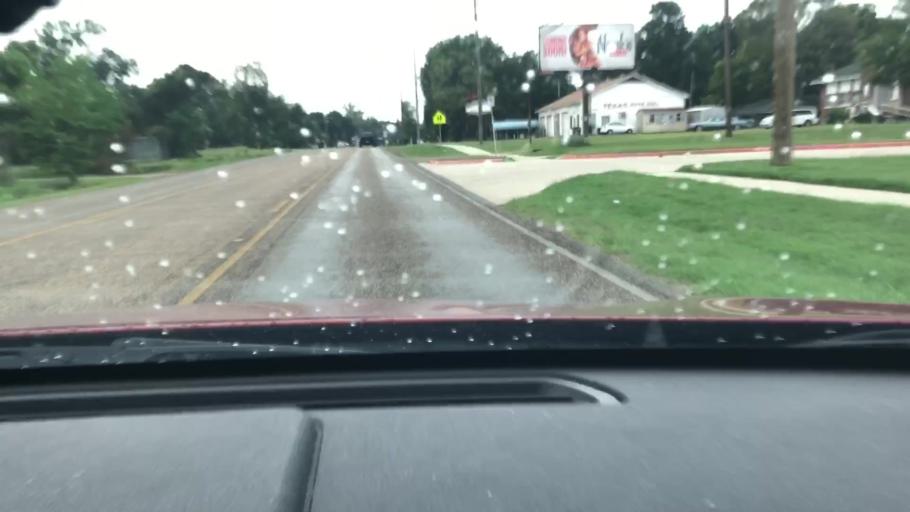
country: US
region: Texas
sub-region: Bowie County
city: Nash
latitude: 33.4429
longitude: -94.1233
